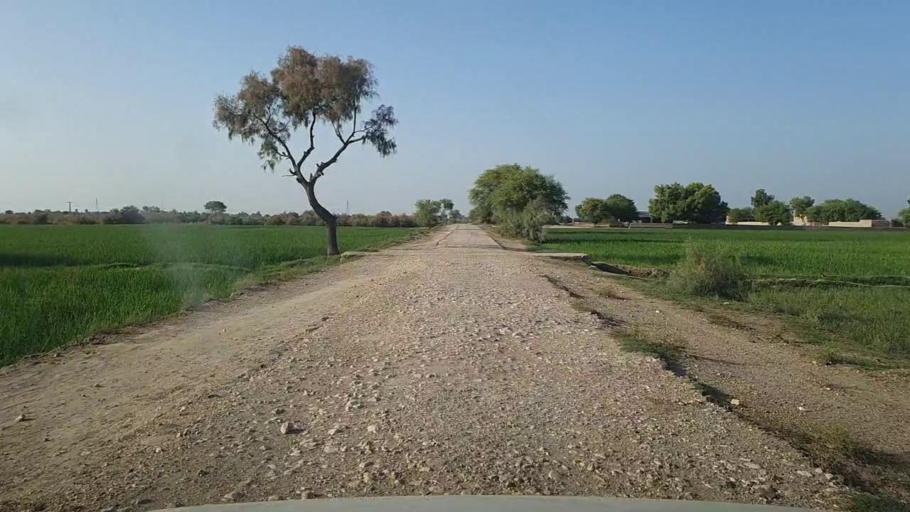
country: PK
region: Sindh
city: Kandhkot
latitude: 28.2991
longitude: 69.3288
